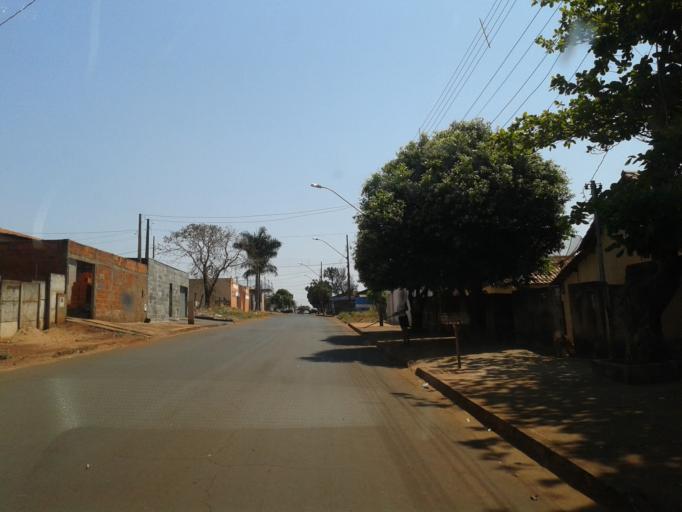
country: BR
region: Minas Gerais
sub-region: Ituiutaba
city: Ituiutaba
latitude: -18.9962
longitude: -49.4441
